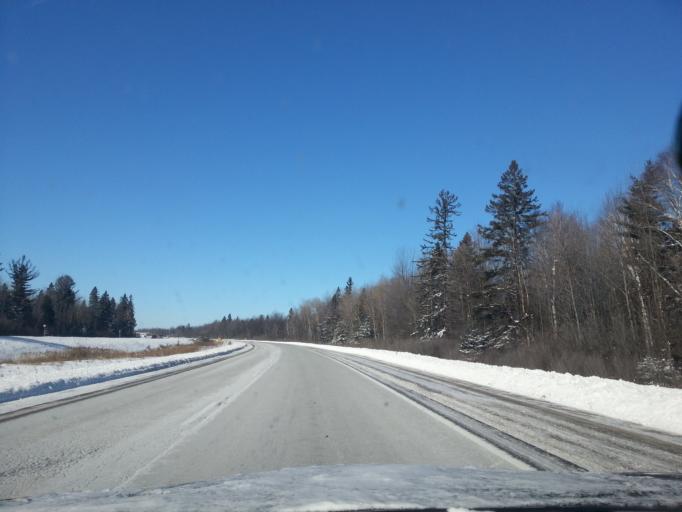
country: CA
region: Ontario
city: Carleton Place
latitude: 45.3091
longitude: -76.0397
